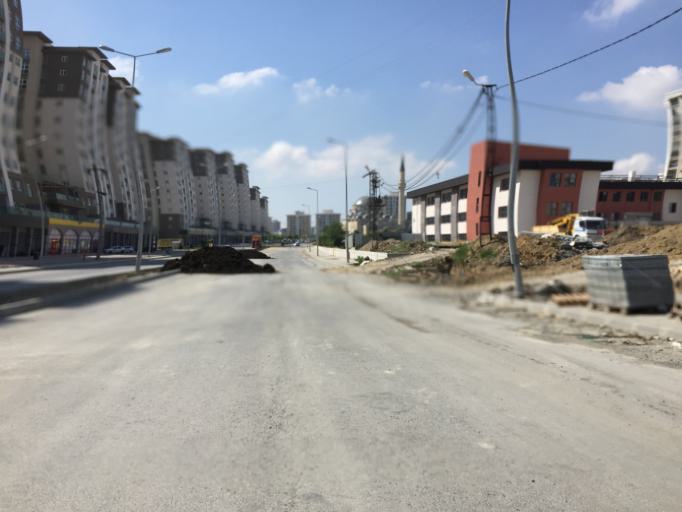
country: TR
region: Istanbul
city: Esenyurt
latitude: 41.0883
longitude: 28.6544
